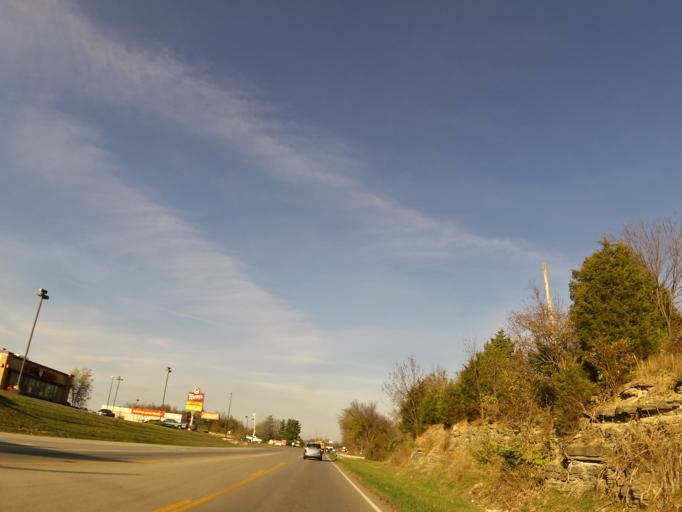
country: US
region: Kentucky
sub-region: Lincoln County
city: Stanford
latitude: 37.5474
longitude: -84.6466
